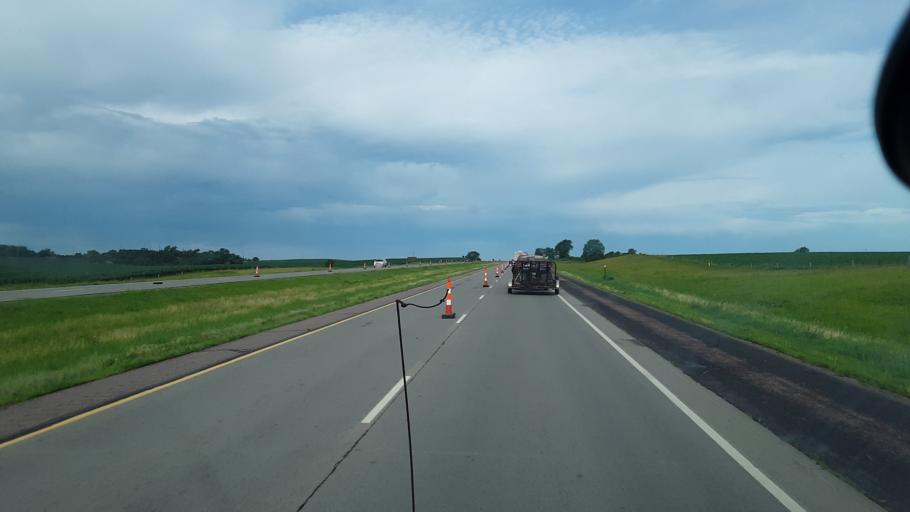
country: US
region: South Dakota
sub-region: Minnehaha County
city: Crooks
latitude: 43.6087
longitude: -96.8552
